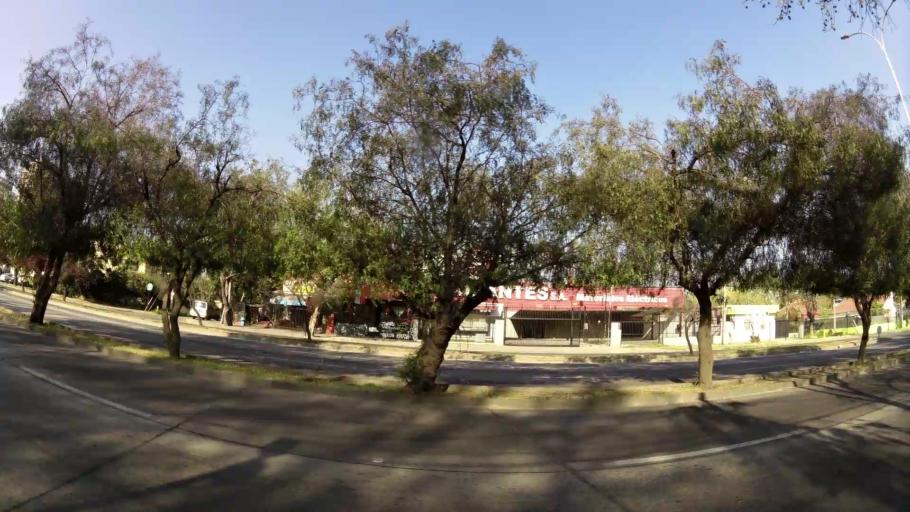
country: CL
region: Santiago Metropolitan
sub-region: Provincia de Santiago
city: Villa Presidente Frei, Nunoa, Santiago, Chile
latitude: -33.4568
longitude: -70.5717
